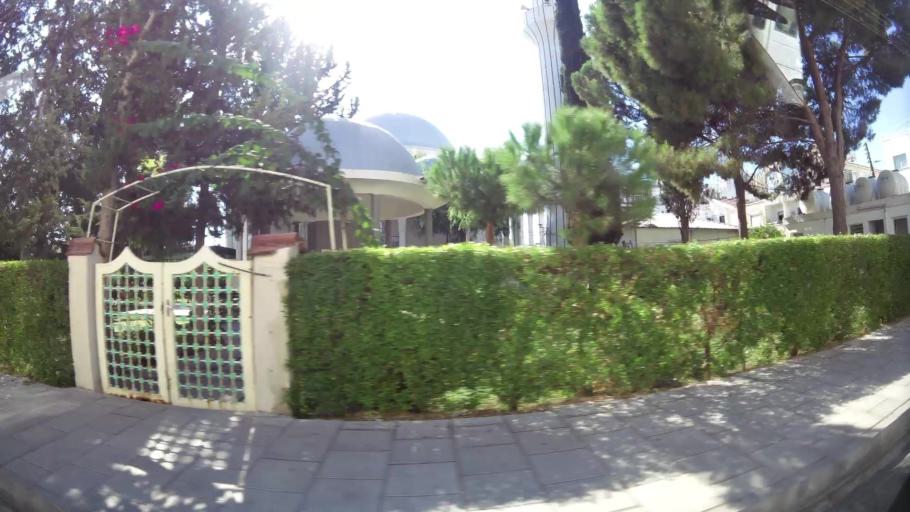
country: CY
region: Lefkosia
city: Nicosia
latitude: 35.2090
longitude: 33.3371
